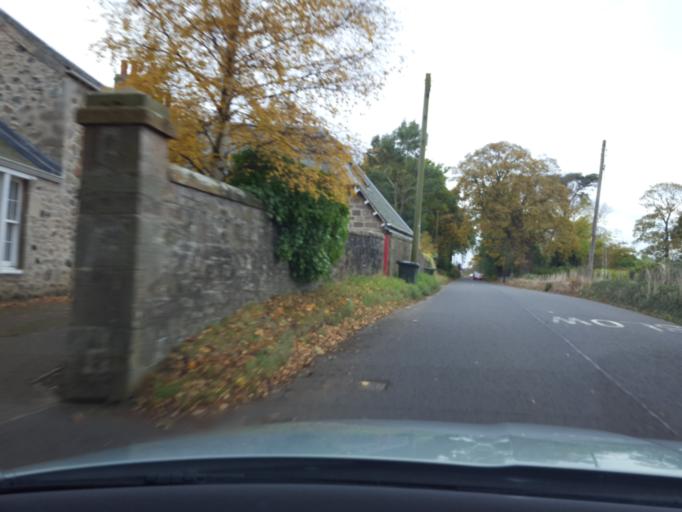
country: GB
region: Scotland
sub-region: Edinburgh
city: Currie
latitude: 55.9218
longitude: -3.3349
